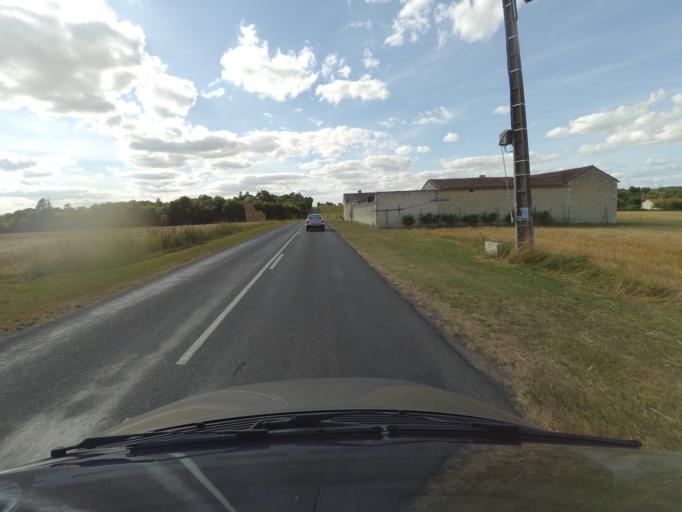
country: FR
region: Poitou-Charentes
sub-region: Departement de la Vienne
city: Saint-Gervais-les-Trois-Clochers
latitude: 46.9551
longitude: 0.4009
